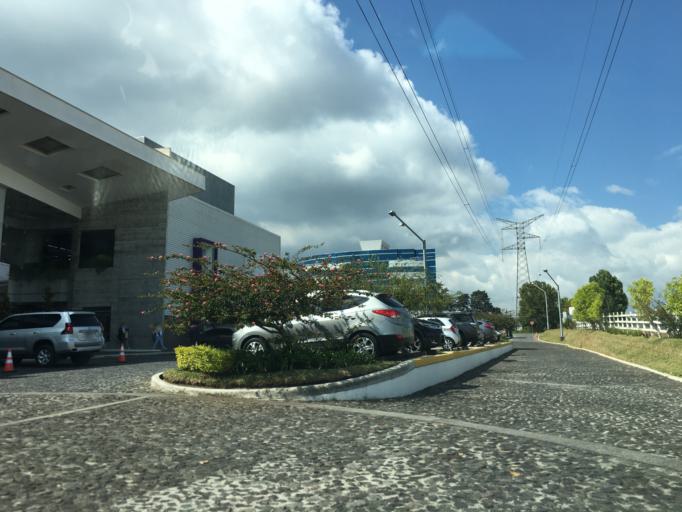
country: GT
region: Guatemala
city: Fraijanes
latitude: 14.4964
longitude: -90.4808
